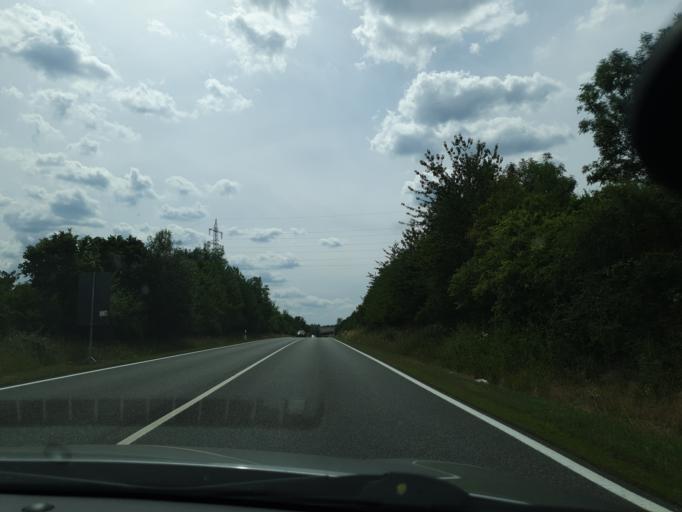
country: DE
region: Rheinland-Pfalz
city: Mayen
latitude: 50.3147
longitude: 7.2312
